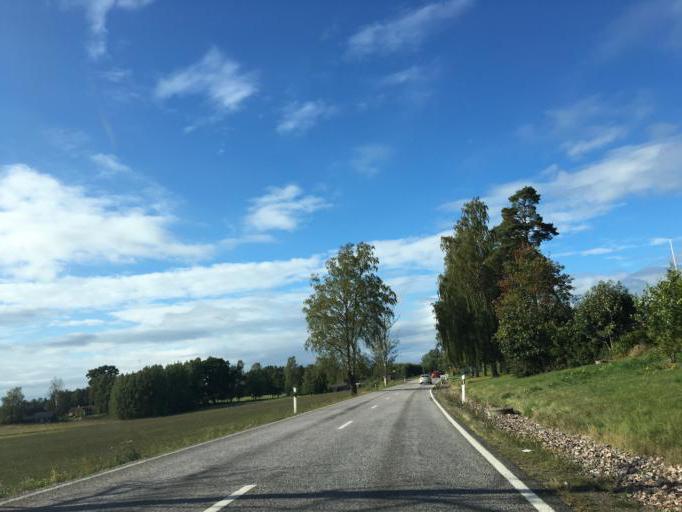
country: SE
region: Soedermanland
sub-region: Nykopings Kommun
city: Stigtomta
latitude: 58.8683
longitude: 16.9006
